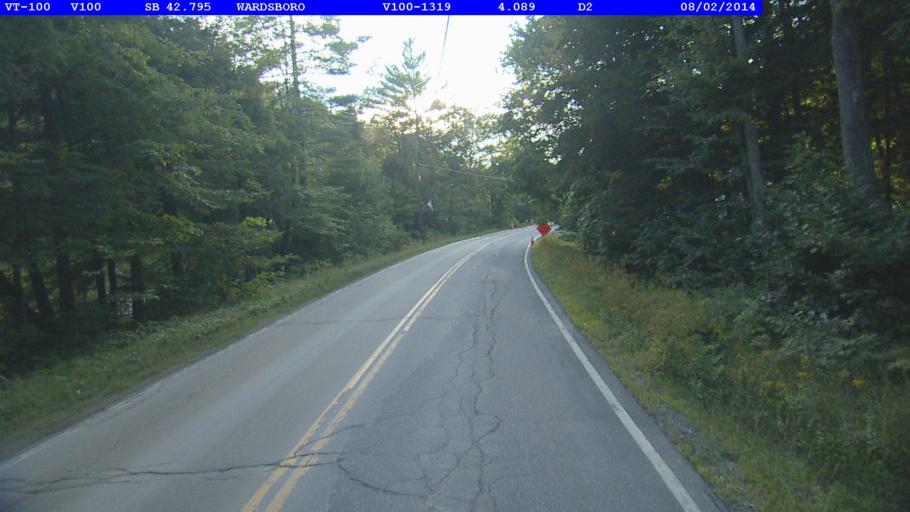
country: US
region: Vermont
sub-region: Windham County
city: Dover
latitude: 43.0253
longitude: -72.8229
